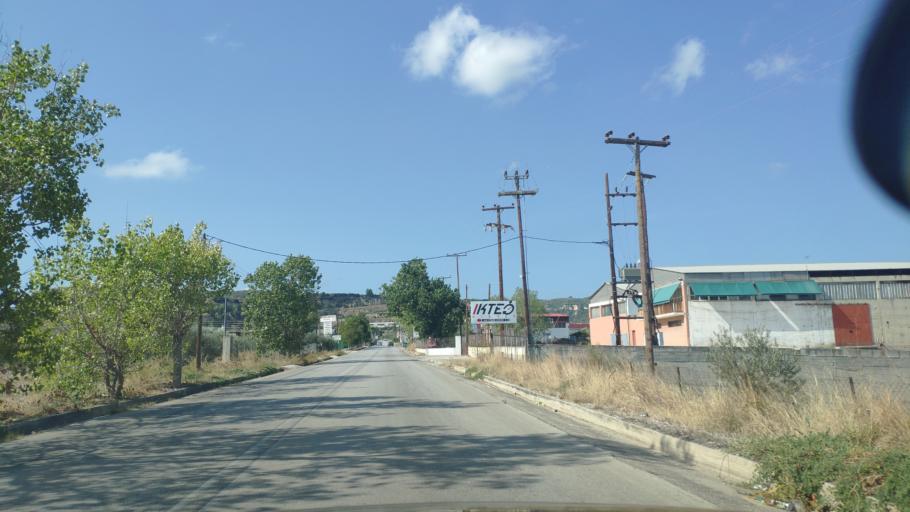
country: GR
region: Peloponnese
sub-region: Nomos Korinthias
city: Pasion
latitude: 38.0040
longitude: 22.7249
